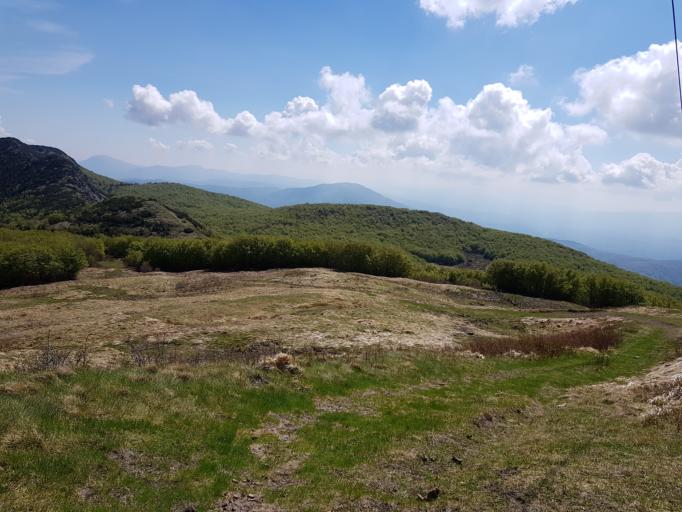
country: IT
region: Liguria
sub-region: Provincia di Genova
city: Santo Stefano d'Aveto
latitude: 44.5563
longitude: 9.4930
